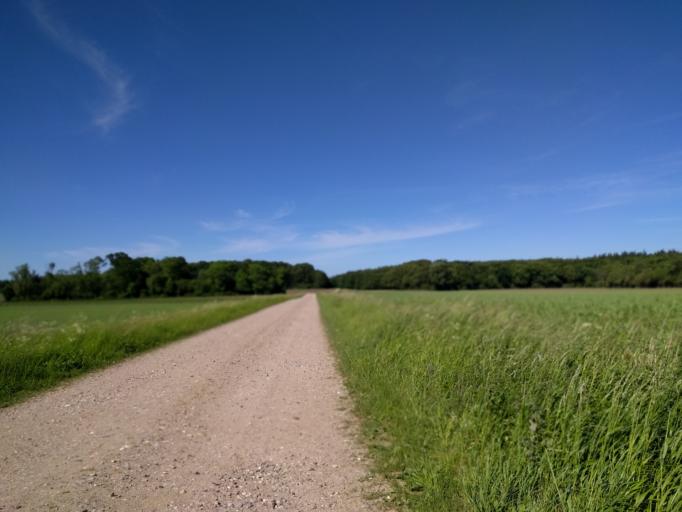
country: DK
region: South Denmark
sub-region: Kerteminde Kommune
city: Kerteminde
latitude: 55.4316
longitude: 10.6662
